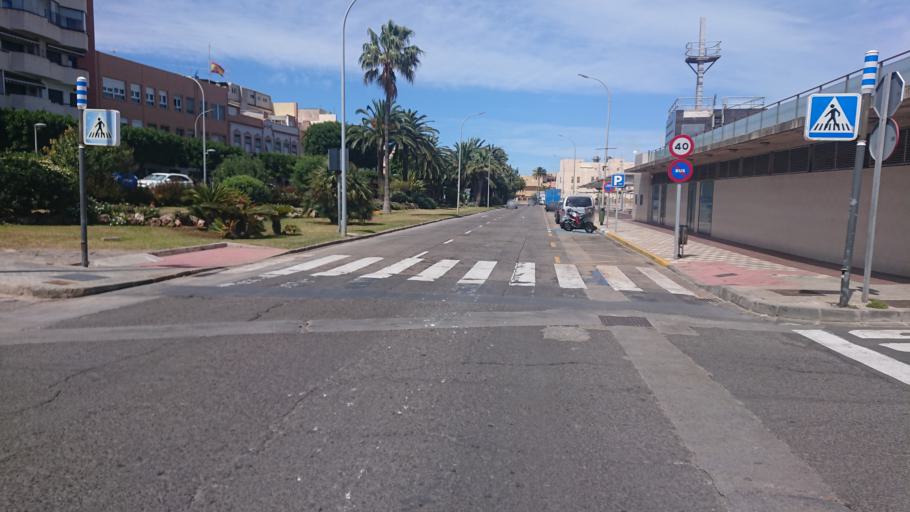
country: ES
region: Melilla
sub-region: Melilla
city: Melilla
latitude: 35.2870
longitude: -2.9411
